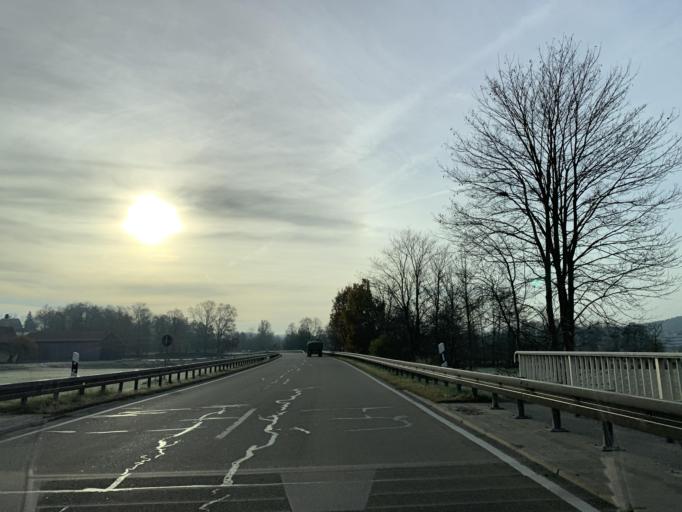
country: DE
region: Bavaria
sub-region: Upper Palatinate
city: Neunburg vorm Wald
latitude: 49.3560
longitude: 12.3753
